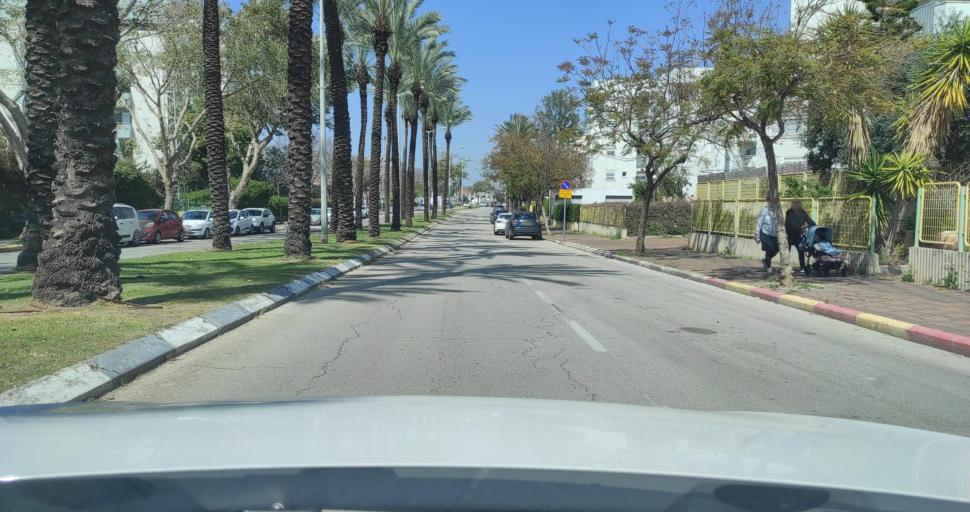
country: IL
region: Central District
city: Nordiyya
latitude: 32.3074
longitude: 34.8809
